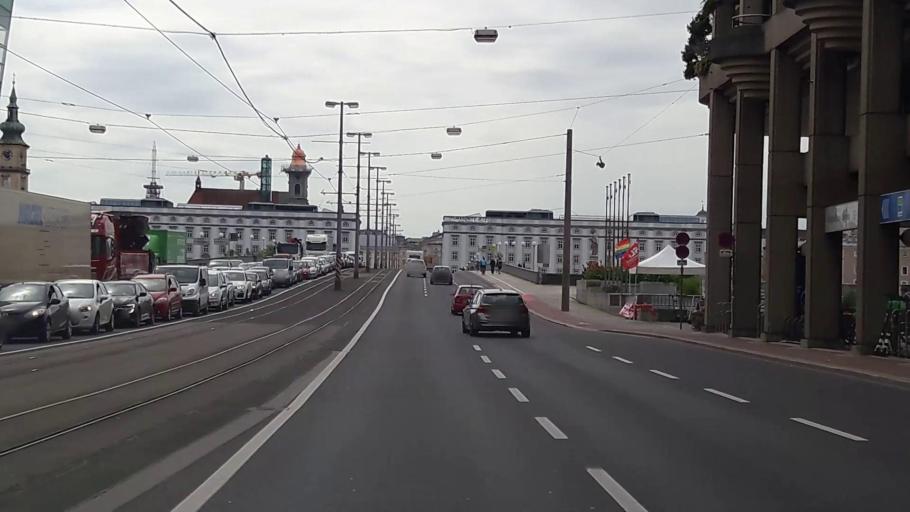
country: AT
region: Upper Austria
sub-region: Linz Stadt
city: Linz
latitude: 48.3102
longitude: 14.2833
